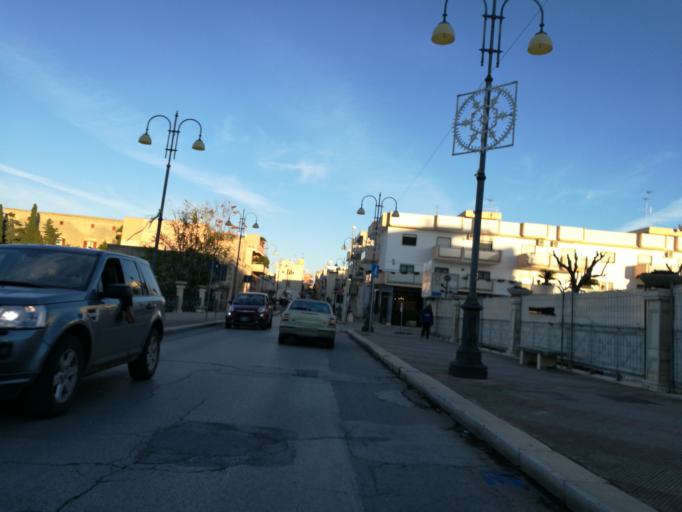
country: IT
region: Apulia
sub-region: Provincia di Bari
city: Adelfia
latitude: 41.0038
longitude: 16.8730
